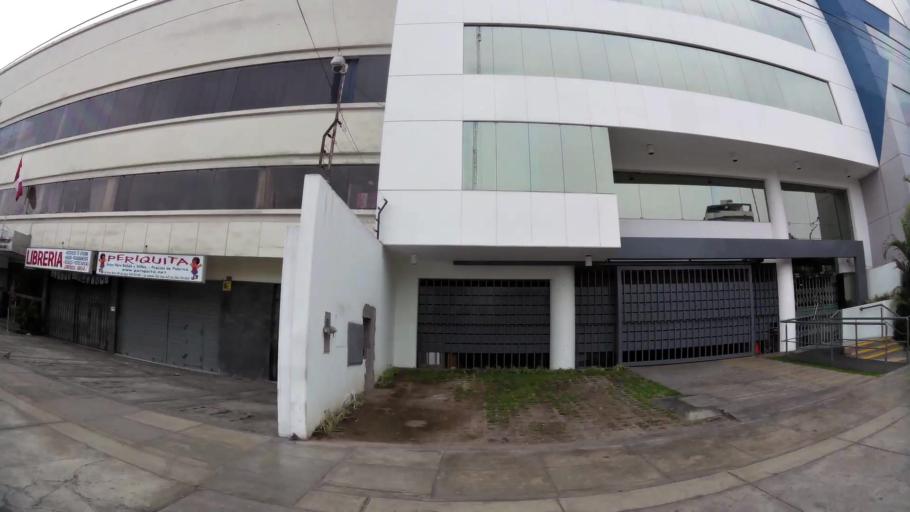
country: PE
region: Lima
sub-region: Lima
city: San Luis
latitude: -12.0983
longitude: -77.0106
